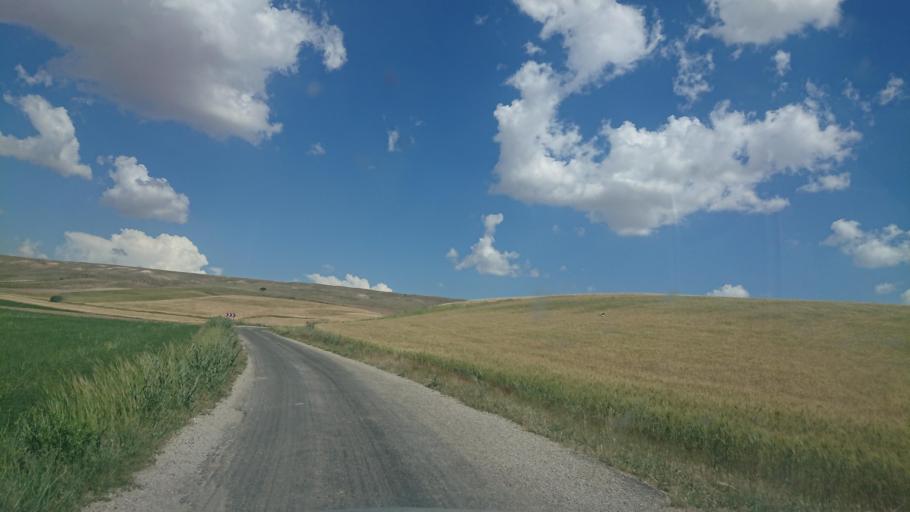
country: TR
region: Aksaray
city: Agacoren
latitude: 38.8134
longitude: 33.7989
